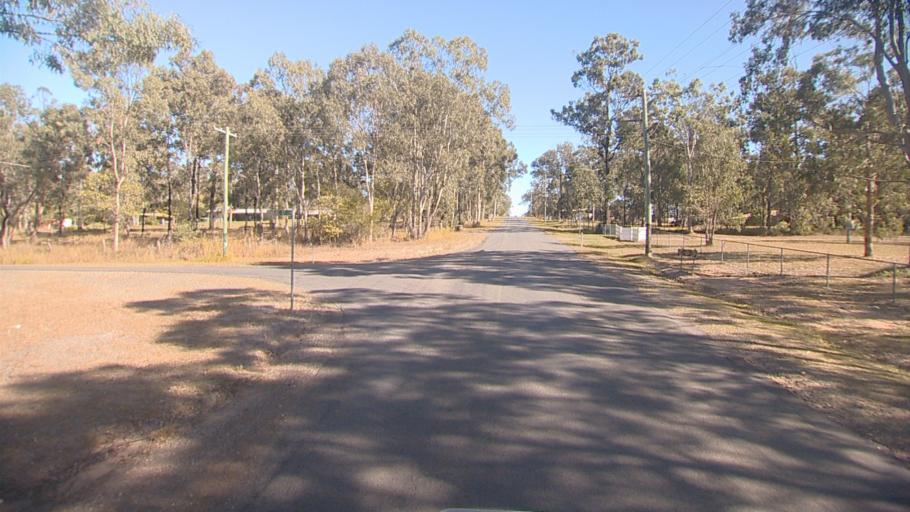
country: AU
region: Queensland
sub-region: Ipswich
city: Springfield Lakes
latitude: -27.7046
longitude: 152.9421
